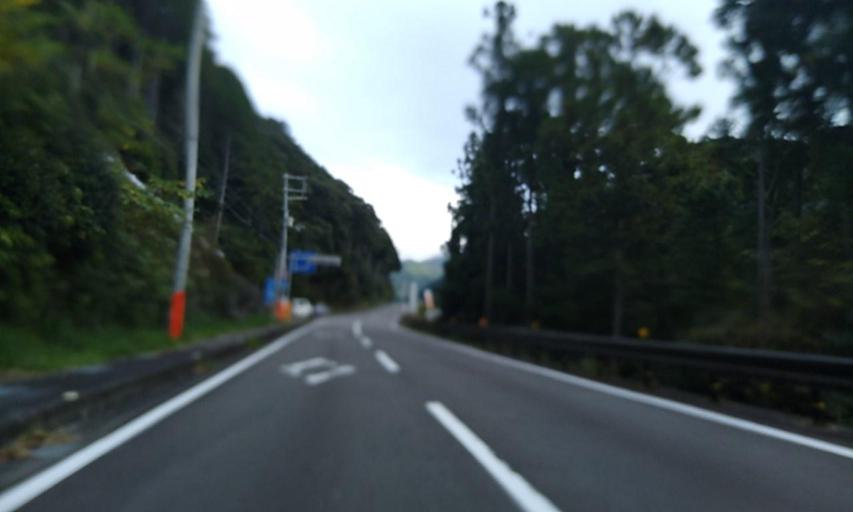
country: JP
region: Wakayama
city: Shingu
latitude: 33.9335
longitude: 135.9704
